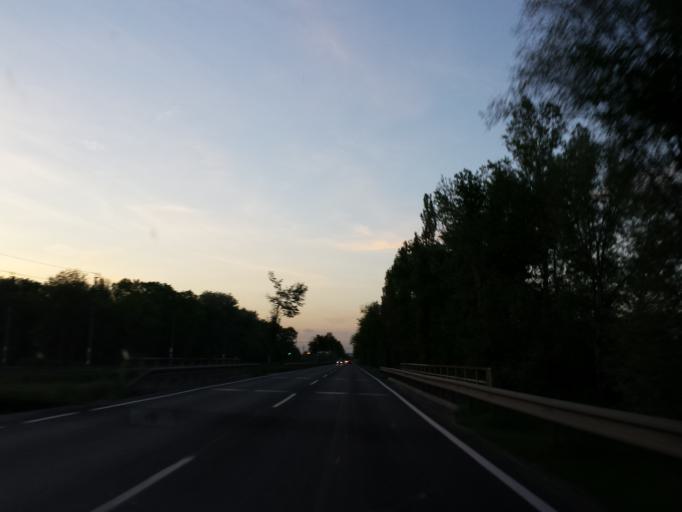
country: AT
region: Lower Austria
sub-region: Politischer Bezirk Tulln
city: Tulln
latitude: 48.3544
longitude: 16.0584
